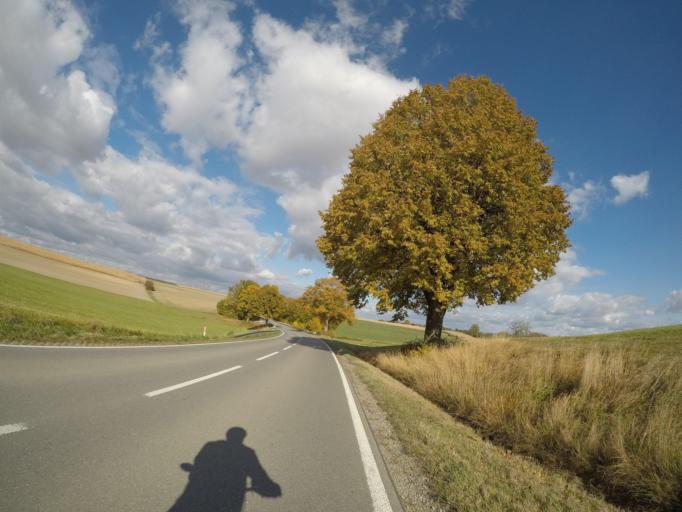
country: DE
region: Baden-Wuerttemberg
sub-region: Tuebingen Region
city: Oberstadion
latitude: 48.1767
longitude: 9.6889
